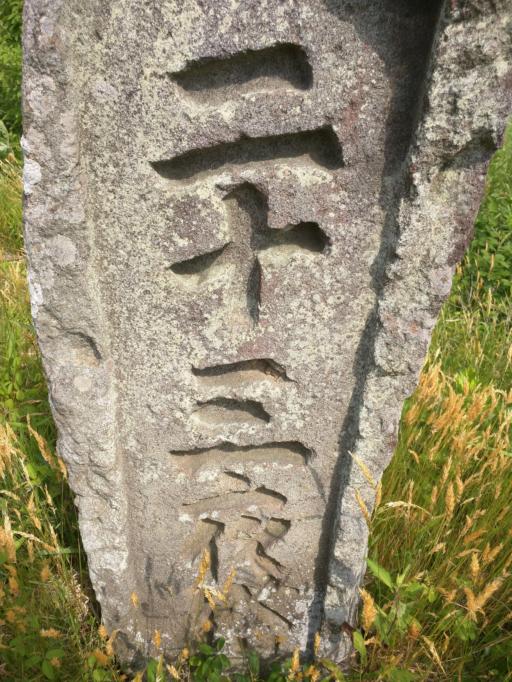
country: JP
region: Tochigi
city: Kuroiso
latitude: 37.0564
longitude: 140.2349
